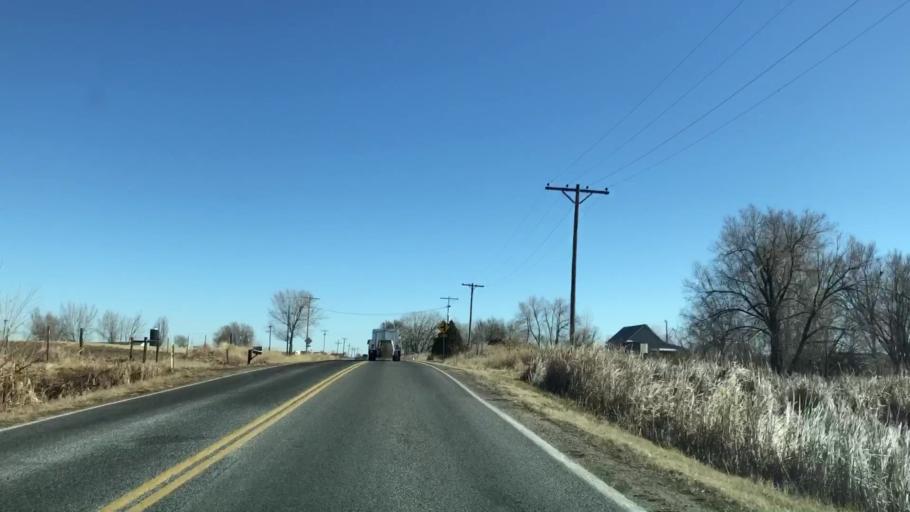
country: US
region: Colorado
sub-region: Weld County
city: Windsor
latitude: 40.4864
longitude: -104.9433
